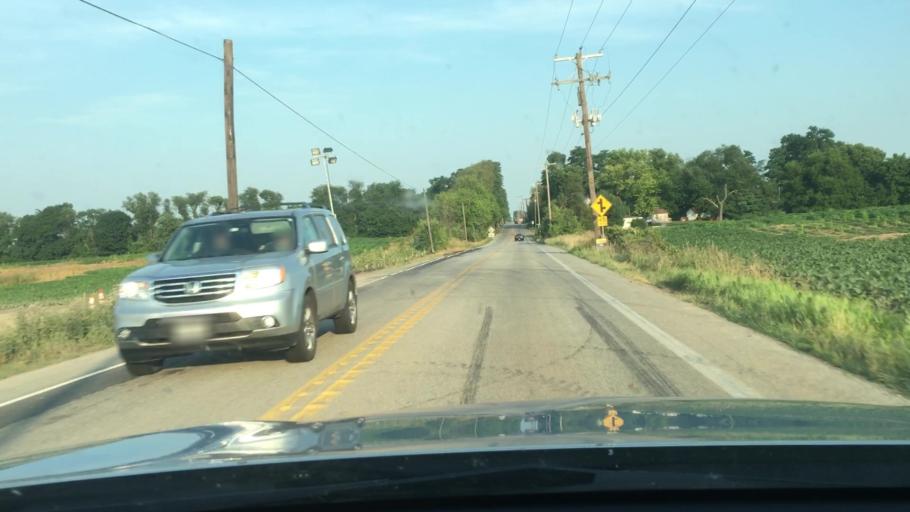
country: US
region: Pennsylvania
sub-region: Cumberland County
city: Boiling Springs
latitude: 40.1796
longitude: -77.1350
